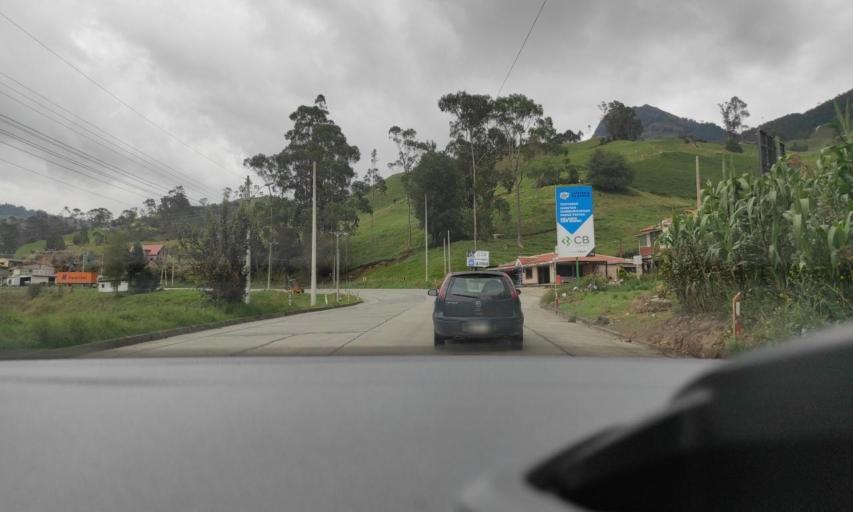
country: EC
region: Canar
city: Azogues
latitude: -2.6734
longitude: -78.8952
